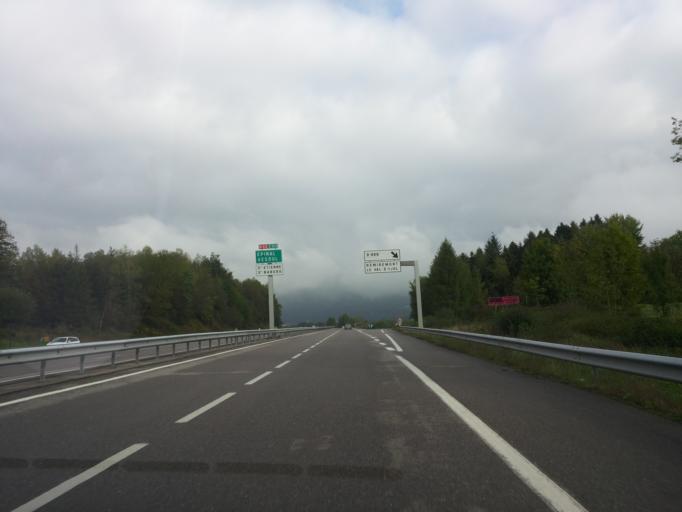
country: FR
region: Lorraine
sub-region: Departement des Vosges
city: Dommartin-les-Remiremont
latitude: 47.9948
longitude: 6.6201
